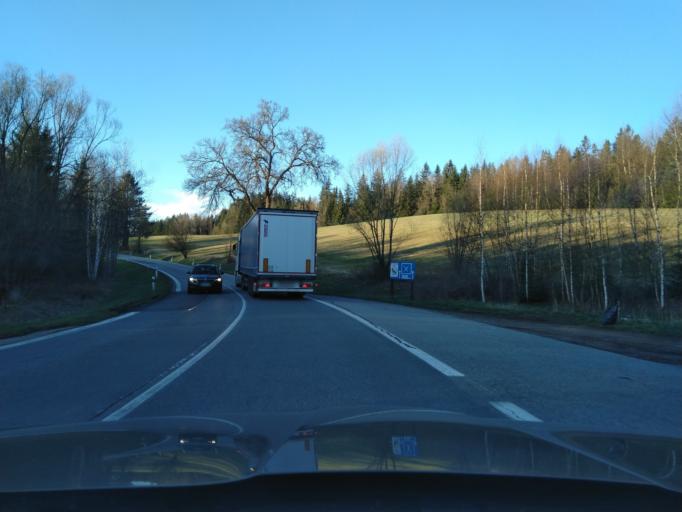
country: CZ
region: Jihocesky
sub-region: Okres Prachatice
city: Vimperk
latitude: 49.0249
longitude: 13.7664
